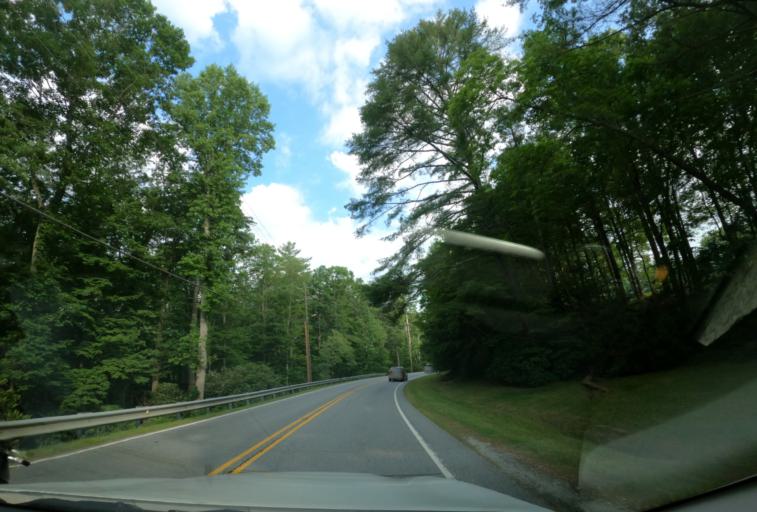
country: US
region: North Carolina
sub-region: Jackson County
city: Cullowhee
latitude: 35.1133
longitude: -83.0296
